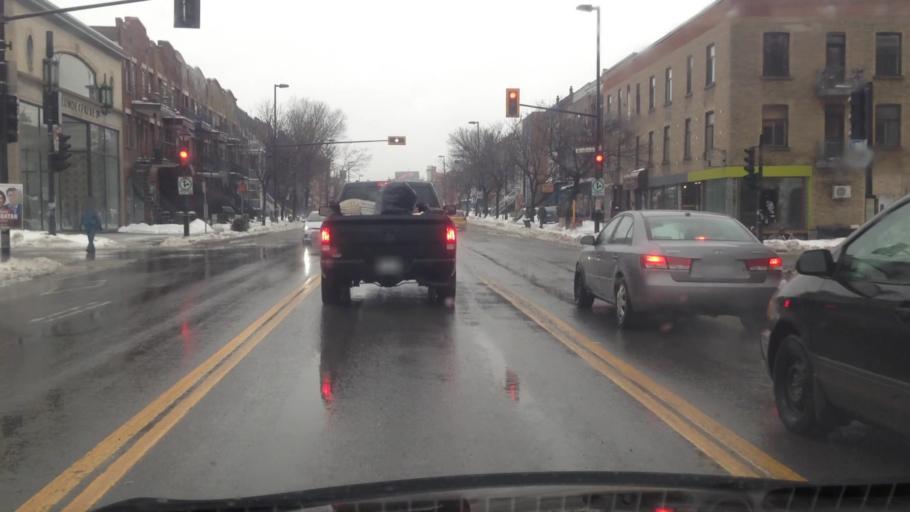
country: CA
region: Quebec
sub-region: Montreal
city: Montreal
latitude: 45.5180
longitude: -73.5922
